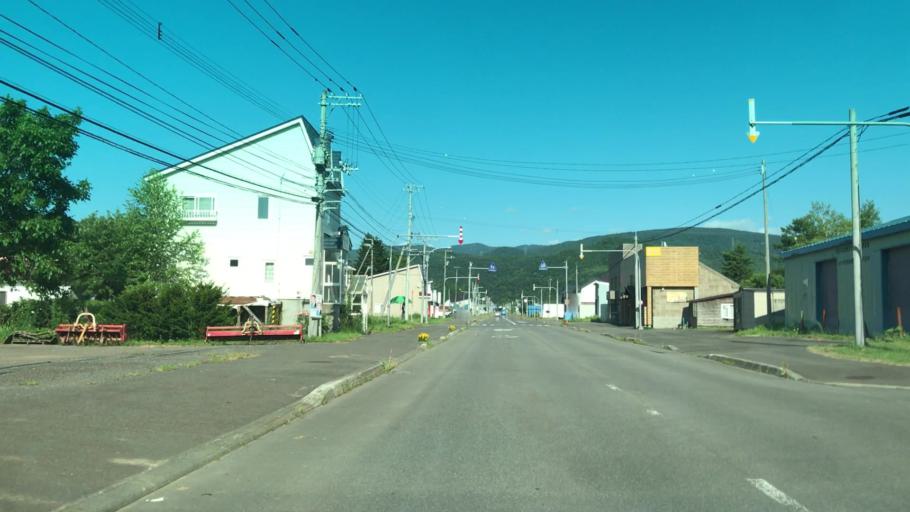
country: JP
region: Hokkaido
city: Yoichi
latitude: 43.0509
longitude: 140.8298
